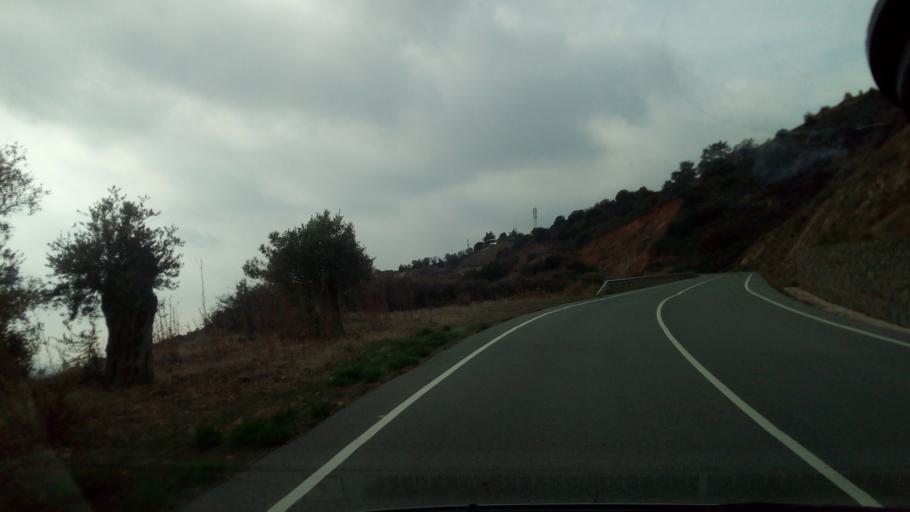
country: CY
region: Lefkosia
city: Lythrodontas
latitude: 34.8764
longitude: 33.2679
